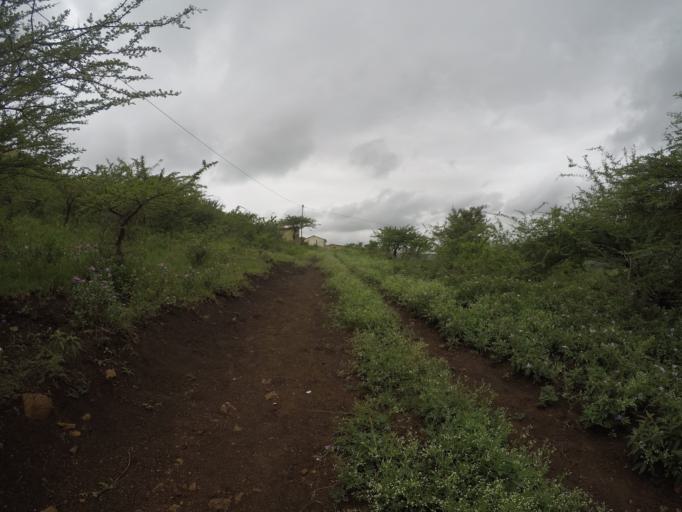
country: ZA
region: KwaZulu-Natal
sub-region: uThungulu District Municipality
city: Empangeni
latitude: -28.6029
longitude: 31.8537
